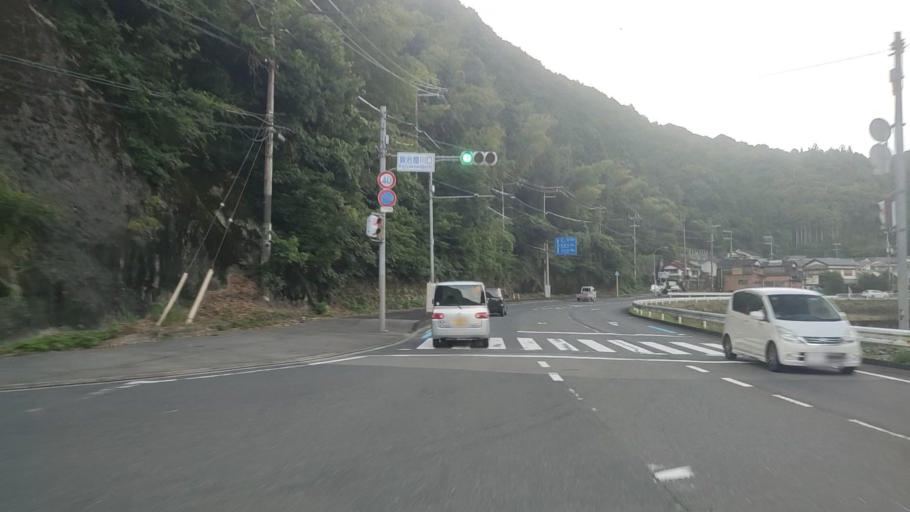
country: JP
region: Wakayama
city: Tanabe
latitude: 33.7880
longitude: 135.5065
